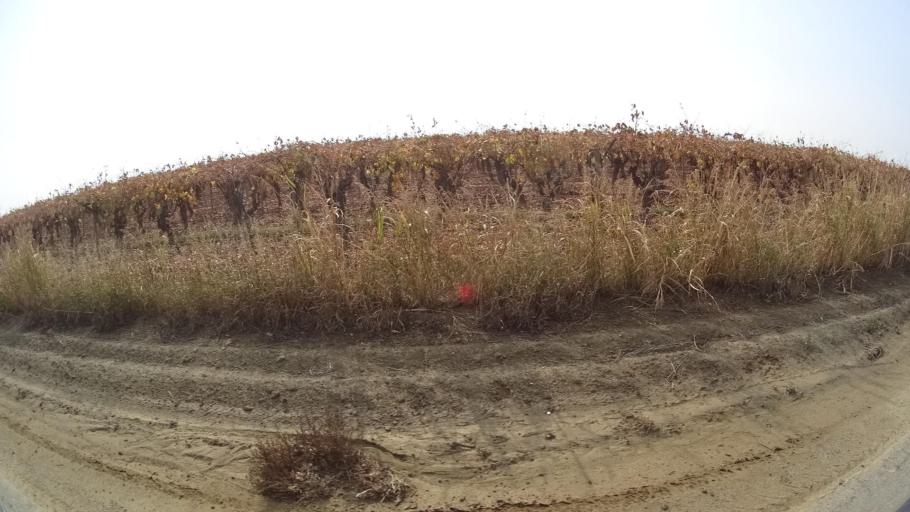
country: US
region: California
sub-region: Kern County
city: Greenfield
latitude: 35.0767
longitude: -119.0842
